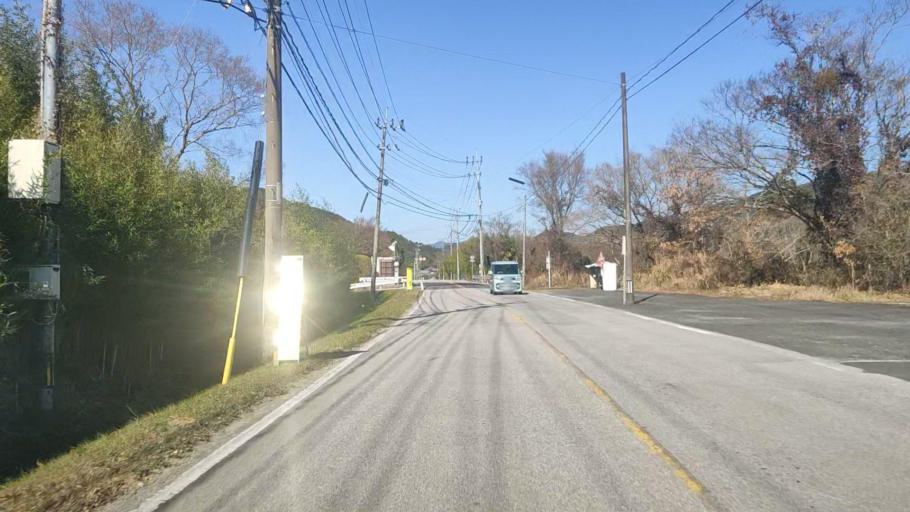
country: JP
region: Oita
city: Saiki
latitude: 32.9102
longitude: 131.9301
